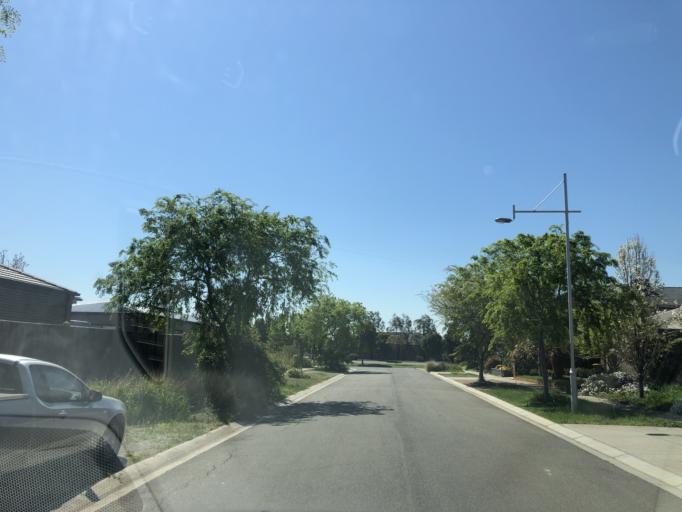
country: AU
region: Victoria
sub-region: Wyndham
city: Point Cook
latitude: -37.8988
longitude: 144.7325
